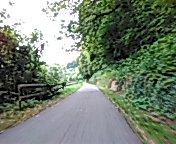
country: LU
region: Grevenmacher
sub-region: Canton d'Echternach
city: Rosport
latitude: 49.7770
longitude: 6.5100
